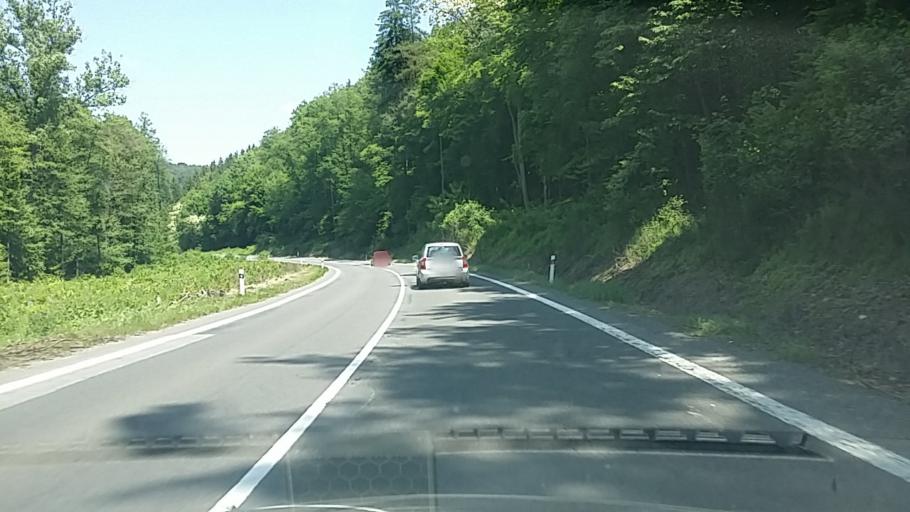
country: SK
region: Banskobystricky
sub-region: Okres Banska Bystrica
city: Zvolen
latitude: 48.5361
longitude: 19.1221
